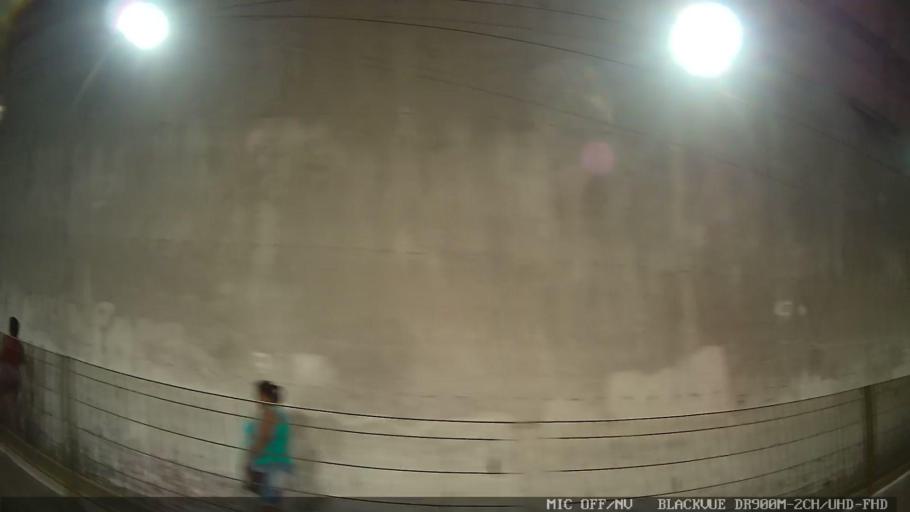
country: BR
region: Sao Paulo
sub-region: Guaruja
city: Guaruja
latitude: -23.9796
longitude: -46.2486
